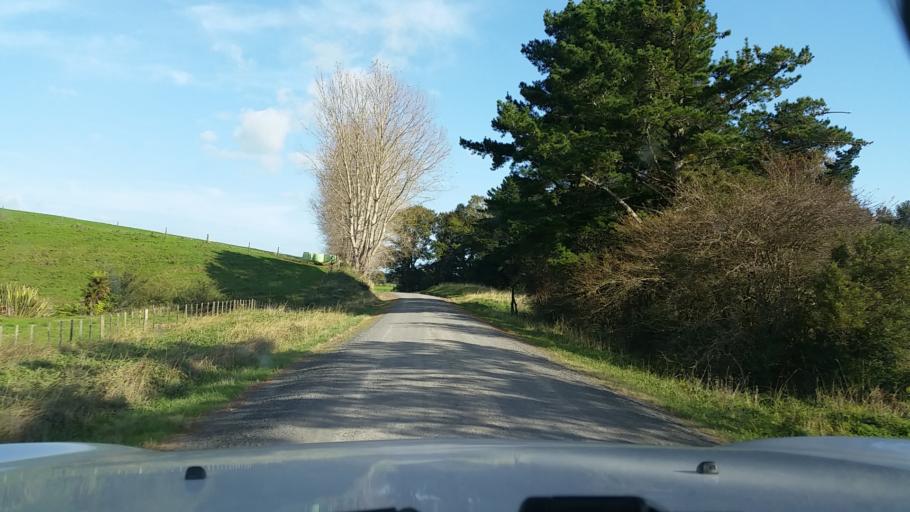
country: NZ
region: Bay of Plenty
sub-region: Western Bay of Plenty District
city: Katikati
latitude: -37.6113
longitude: 175.7961
